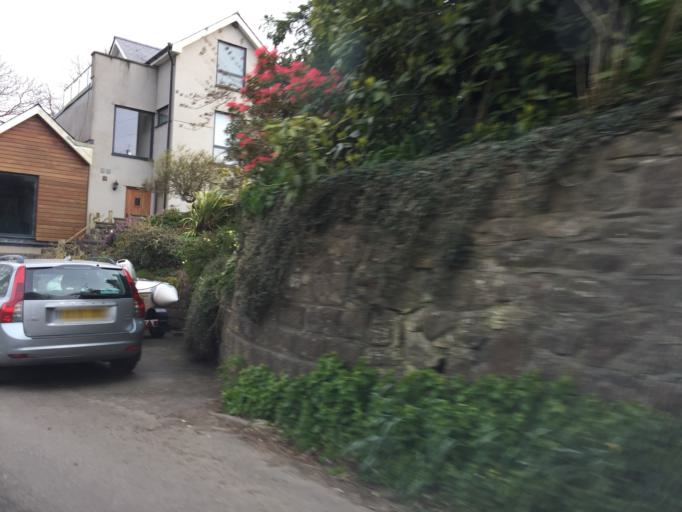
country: GB
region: Wales
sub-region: Cardiff
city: Radyr
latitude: 51.5370
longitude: -3.2313
